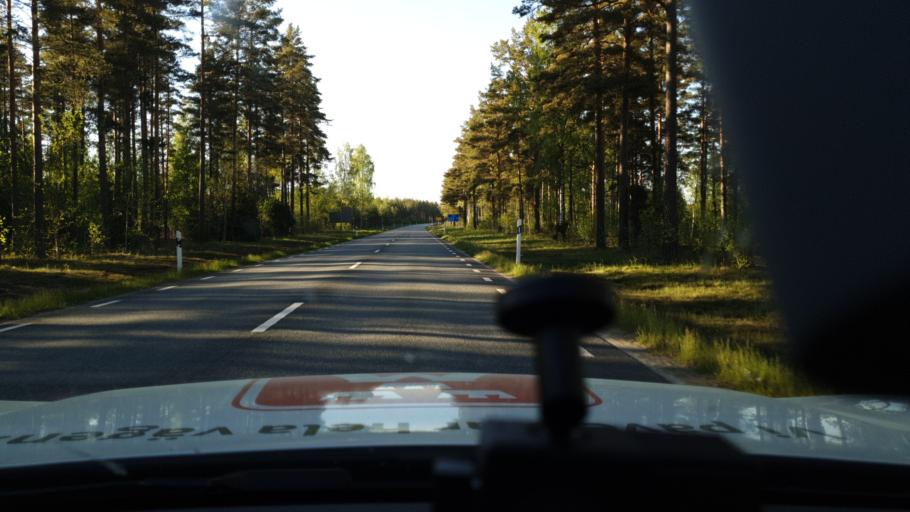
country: SE
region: Joenkoeping
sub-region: Eksjo Kommun
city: Eksjoe
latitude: 57.6038
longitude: 14.9694
